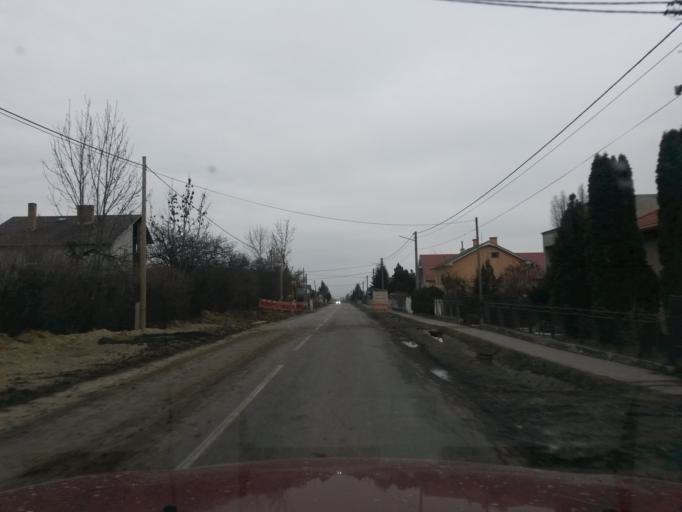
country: SK
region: Kosicky
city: Trebisov
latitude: 48.6974
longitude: 21.8081
